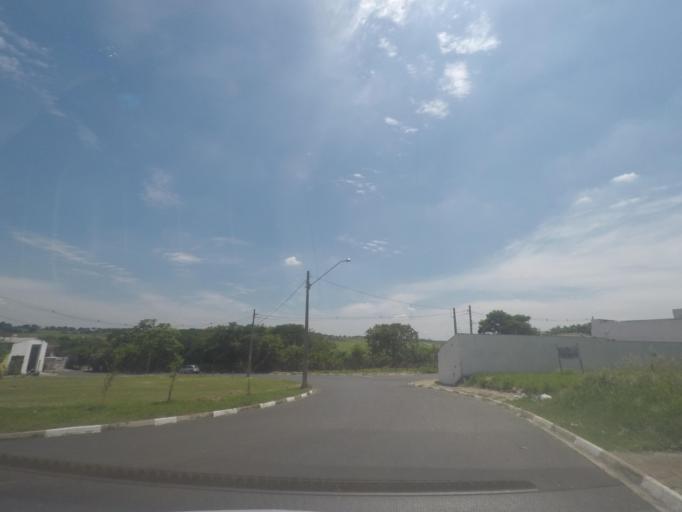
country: BR
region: Sao Paulo
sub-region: Sumare
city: Sumare
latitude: -22.7977
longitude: -47.2704
